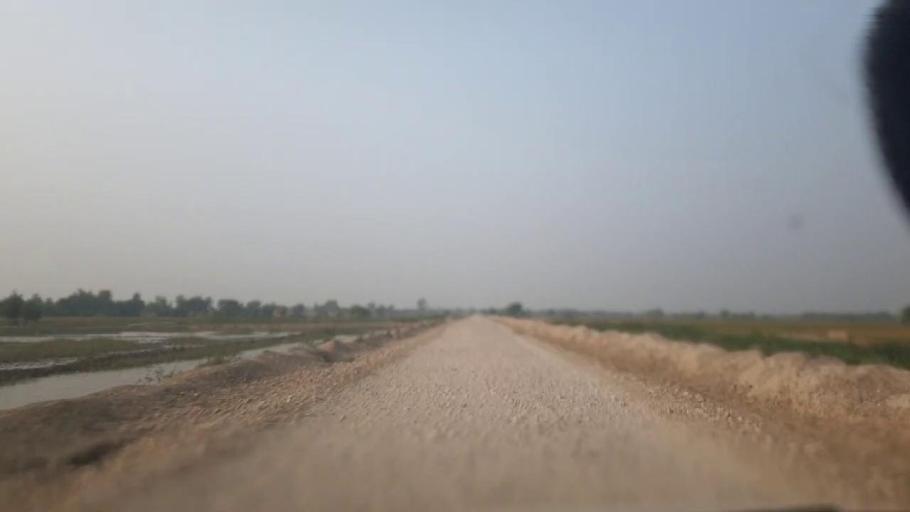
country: PK
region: Sindh
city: Bulri
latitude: 24.7935
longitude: 68.4173
